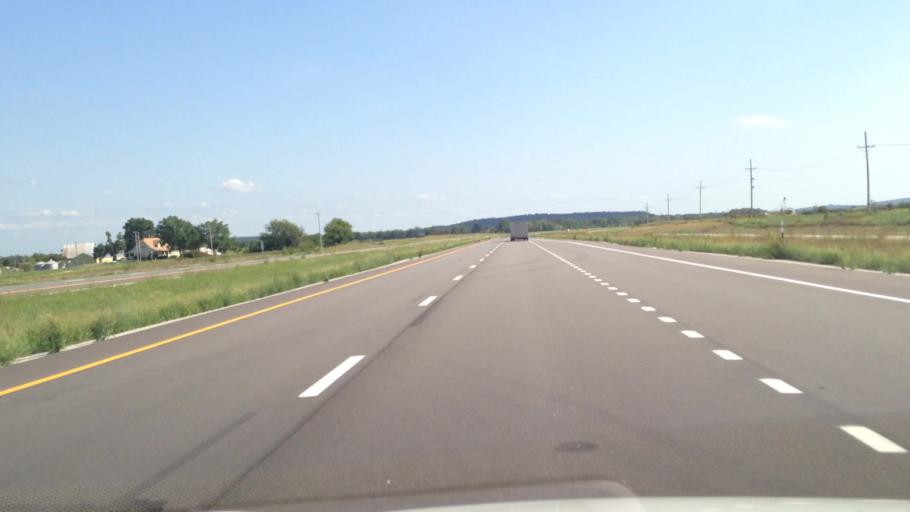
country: US
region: Kansas
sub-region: Linn County
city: La Cygne
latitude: 38.3405
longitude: -94.6806
